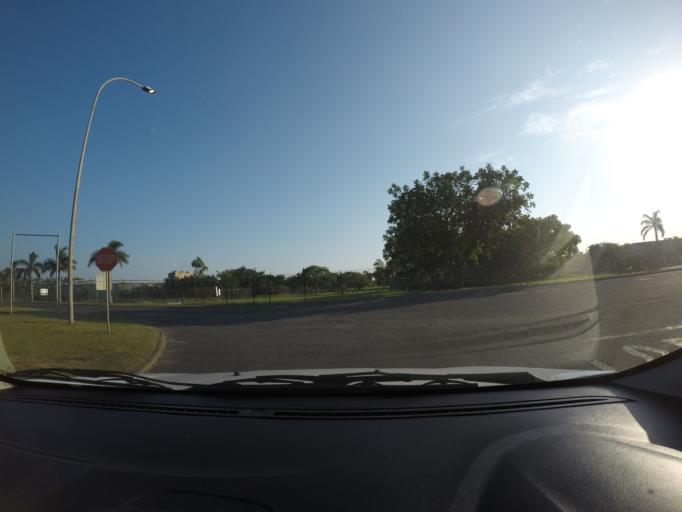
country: ZA
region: KwaZulu-Natal
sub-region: uThungulu District Municipality
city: Richards Bay
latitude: -28.7639
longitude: 31.9964
